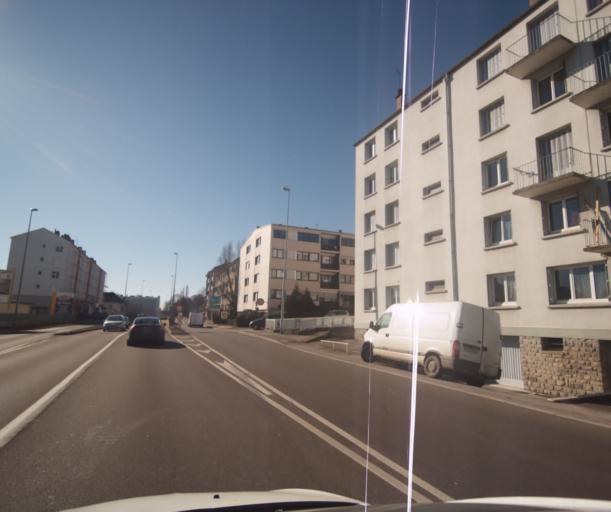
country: FR
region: Franche-Comte
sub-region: Departement du Doubs
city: Besancon
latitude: 47.2545
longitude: 6.0175
